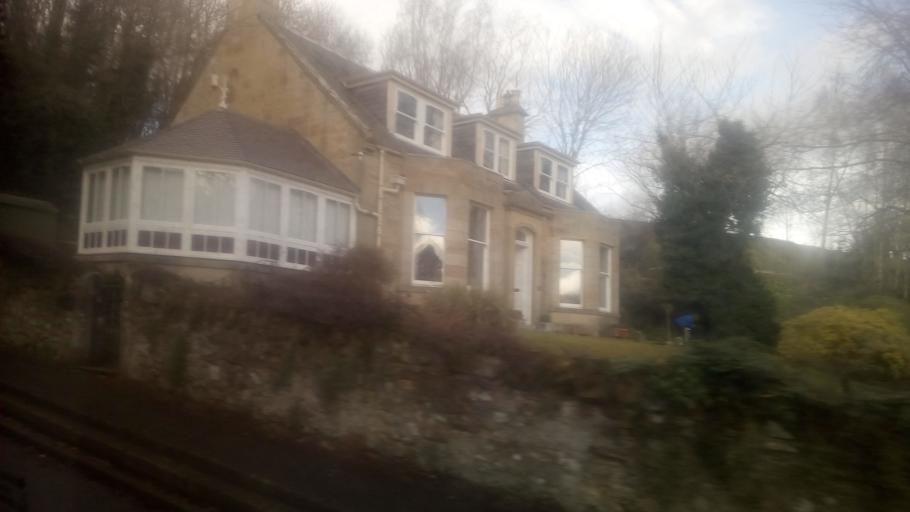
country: GB
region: Scotland
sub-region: Fife
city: Pathhead
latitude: 55.8693
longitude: -2.9804
